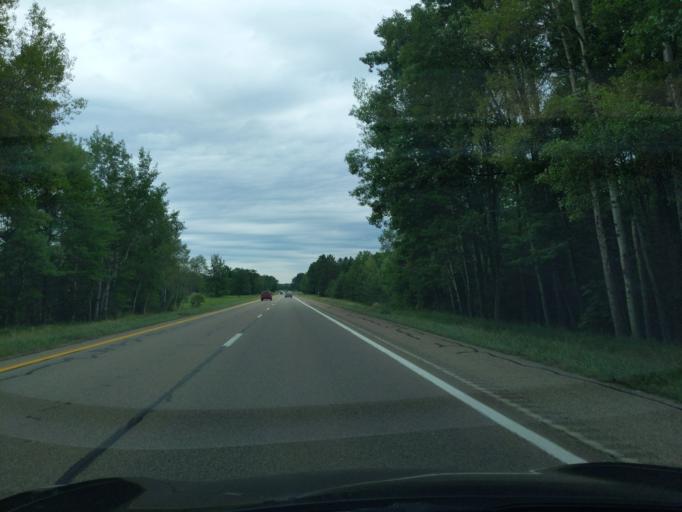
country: US
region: Michigan
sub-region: Roscommon County
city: Houghton Lake
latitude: 44.3217
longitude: -84.8072
